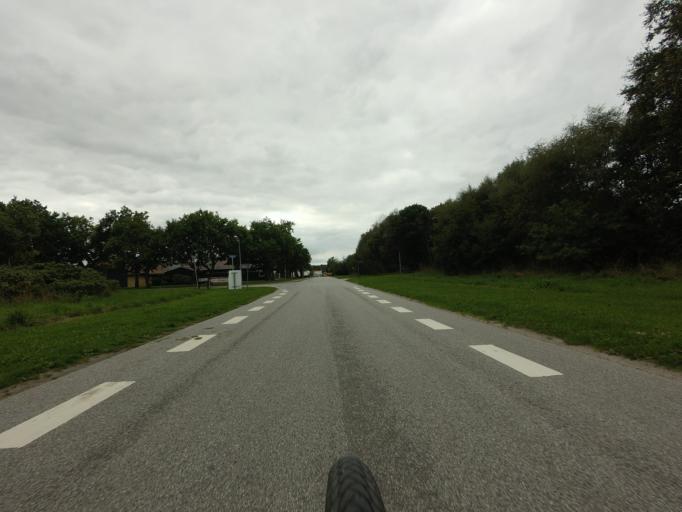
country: DK
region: North Denmark
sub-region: Hjorring Kommune
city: Sindal
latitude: 57.5871
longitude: 10.1916
